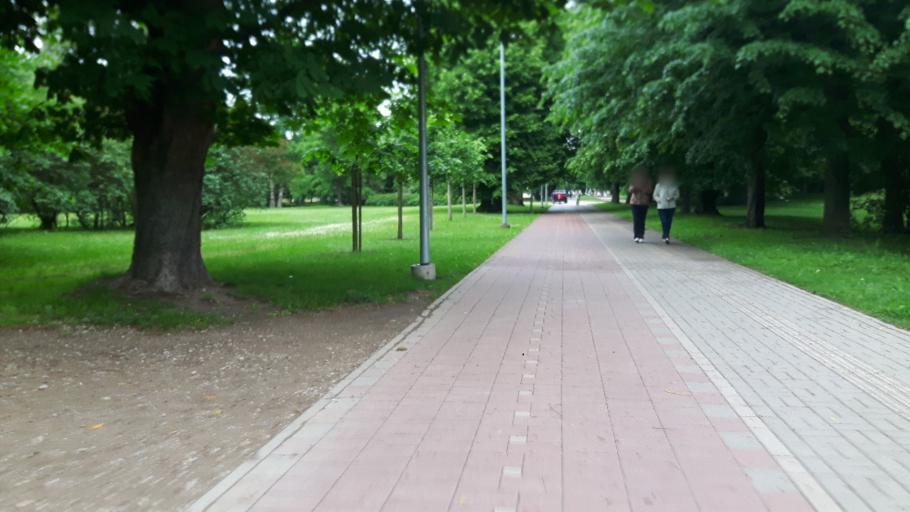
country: LV
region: Liepaja
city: Liepaja
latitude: 56.5084
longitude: 20.9936
